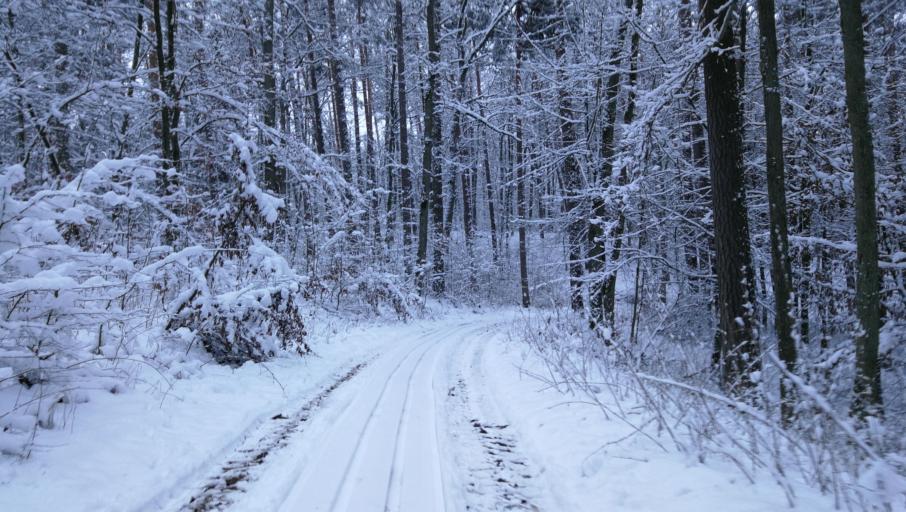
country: PL
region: Kujawsko-Pomorskie
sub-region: Powiat brodnicki
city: Gorzno
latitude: 53.2045
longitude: 19.6976
